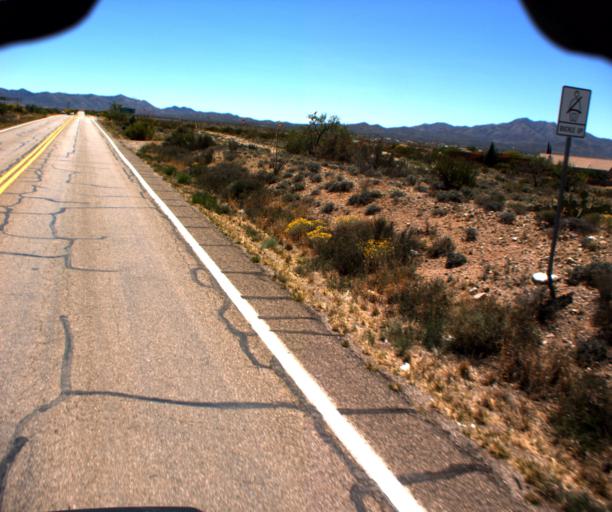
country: US
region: Arizona
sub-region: Pima County
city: Vail
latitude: 32.0025
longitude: -110.6891
